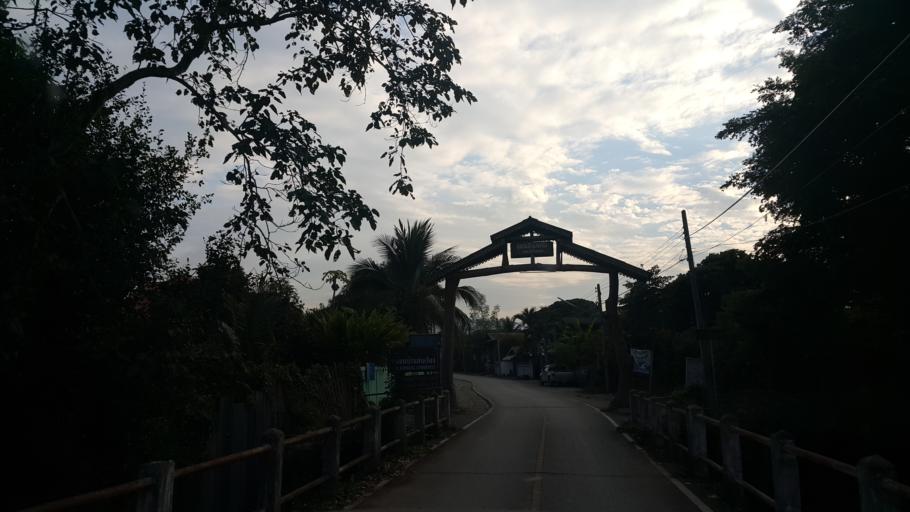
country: TH
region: Lampang
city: Sop Prap
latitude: 17.8693
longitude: 99.3313
